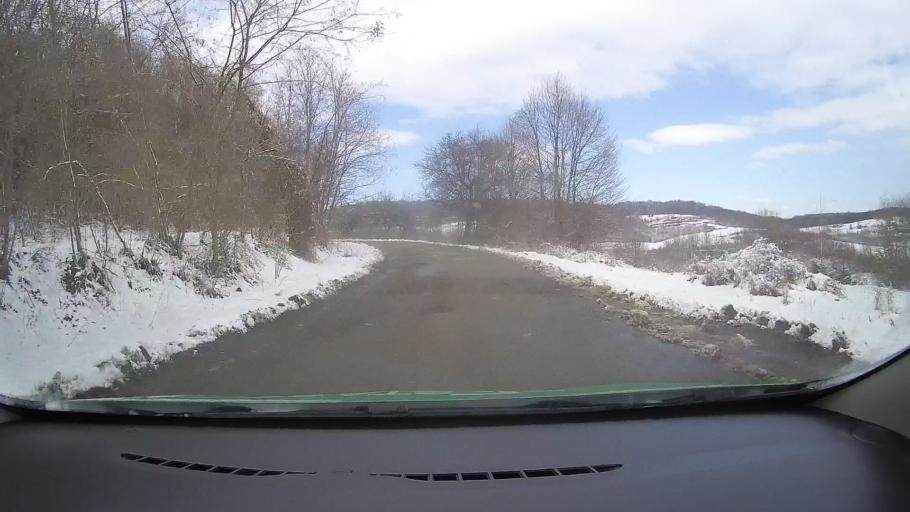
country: RO
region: Sibiu
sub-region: Comuna Altina
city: Altina
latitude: 45.9910
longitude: 24.4335
